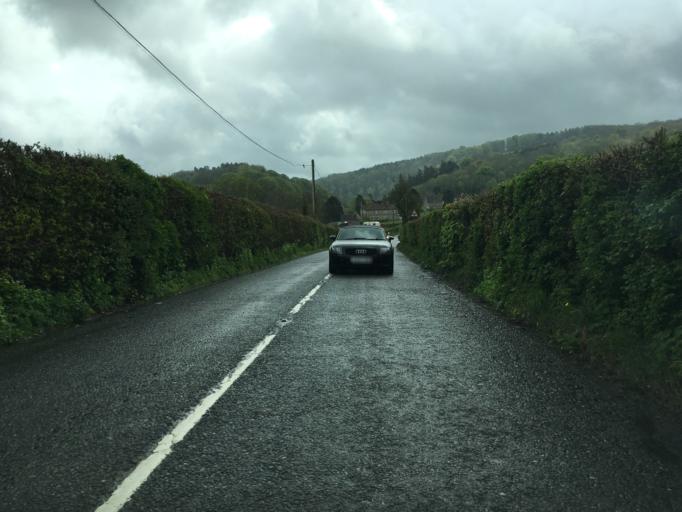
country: GB
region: England
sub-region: North Somerset
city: Burrington
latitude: 51.3337
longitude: -2.7439
